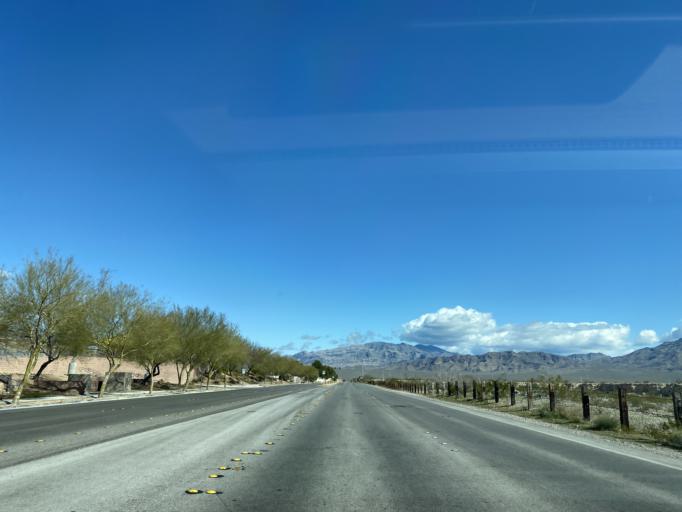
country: US
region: Nevada
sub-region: Clark County
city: North Las Vegas
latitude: 36.3225
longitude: -115.2785
